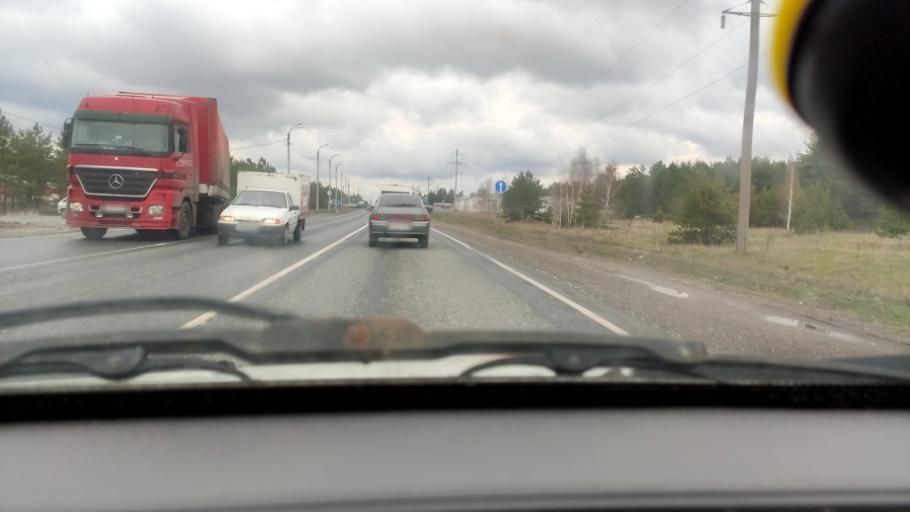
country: RU
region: Samara
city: Zhigulevsk
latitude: 53.5644
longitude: 49.5454
